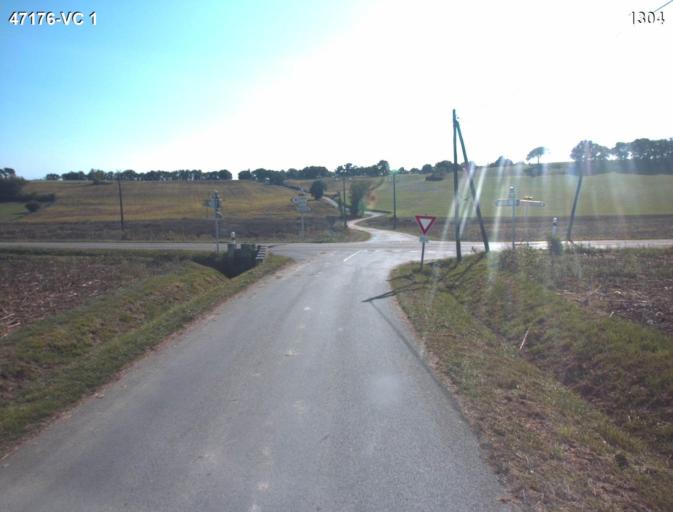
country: FR
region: Aquitaine
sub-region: Departement du Lot-et-Garonne
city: Lavardac
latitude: 44.2042
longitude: 0.2940
